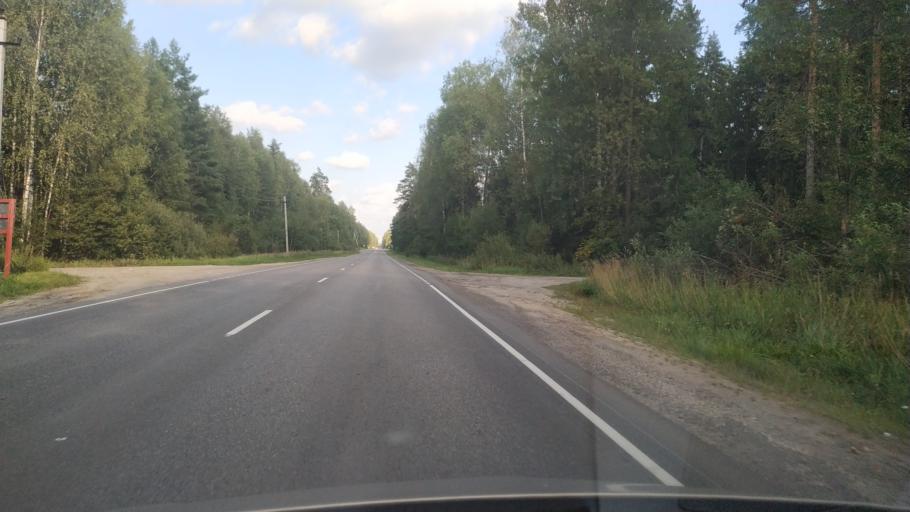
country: RU
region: Moskovskaya
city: Vereya
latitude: 55.7031
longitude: 39.1762
